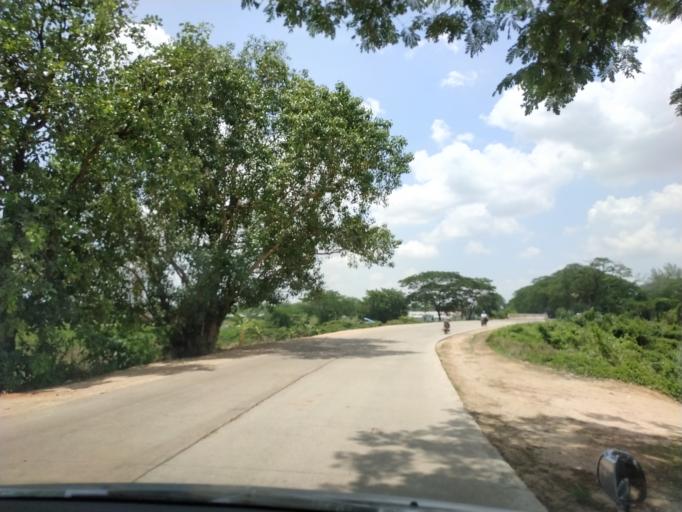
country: MM
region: Bago
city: Bago
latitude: 17.4768
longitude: 96.5096
